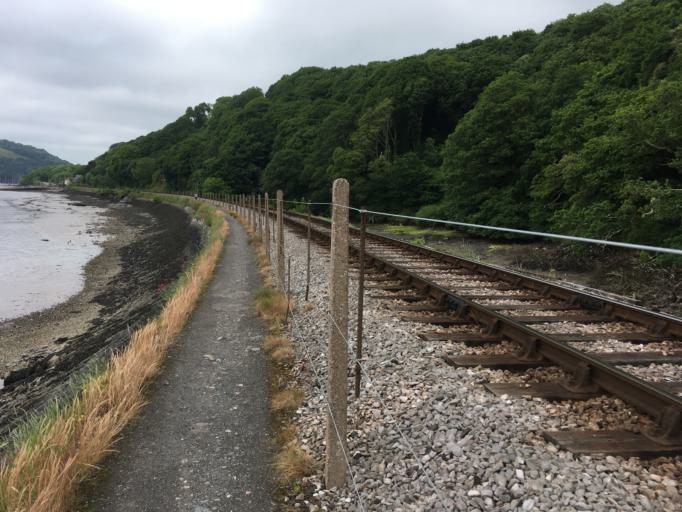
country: GB
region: England
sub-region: Devon
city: Dartmouth
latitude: 50.3559
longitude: -3.5701
